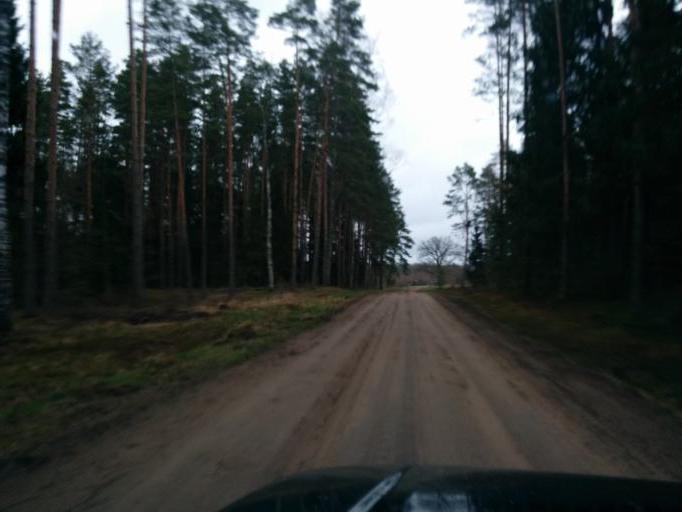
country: LV
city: Tireli
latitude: 56.7948
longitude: 23.6614
